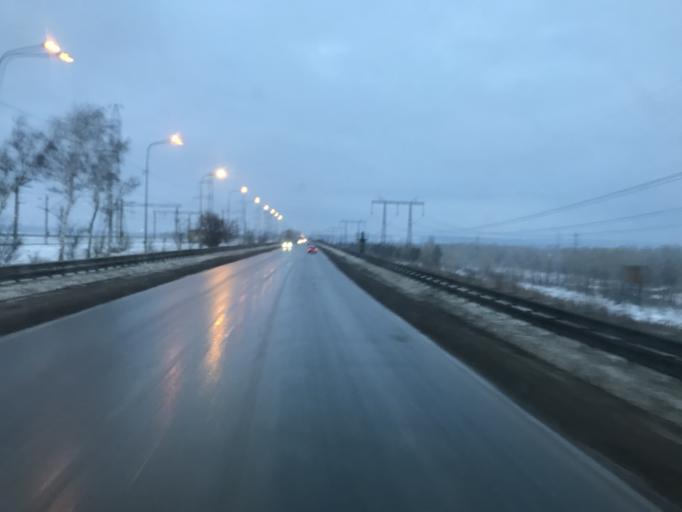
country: RU
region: Samara
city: Zhigulevsk
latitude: 53.4402
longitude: 49.4804
